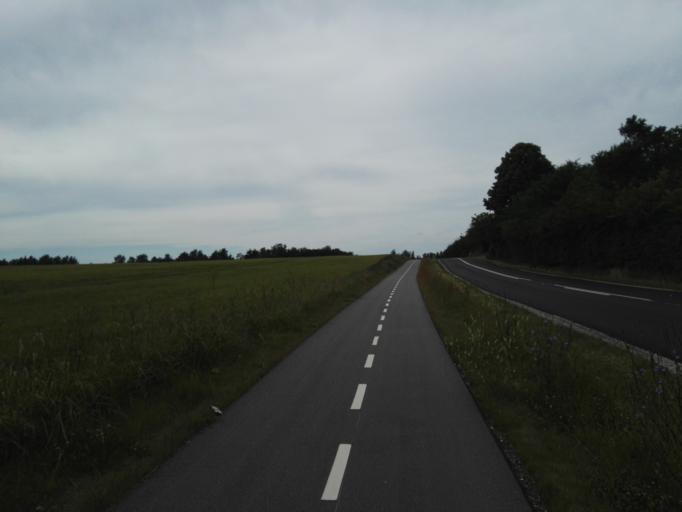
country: DK
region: Capital Region
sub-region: Hillerod Kommune
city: Skaevinge
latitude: 55.9167
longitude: 12.1878
